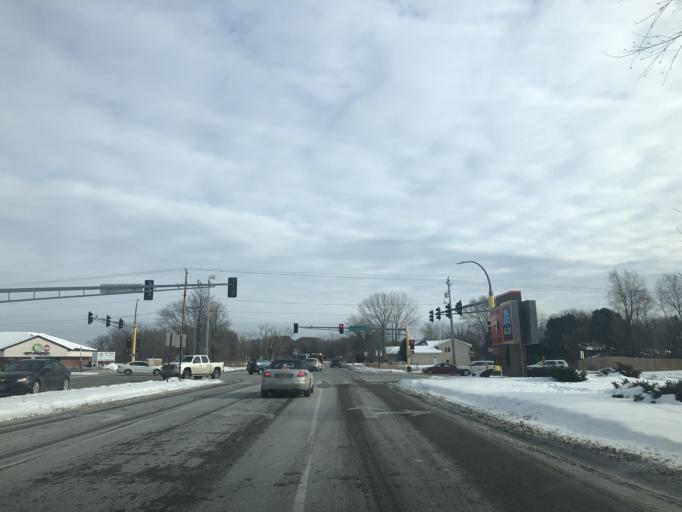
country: US
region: Minnesota
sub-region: Anoka County
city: Lexington
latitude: 45.1566
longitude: -93.1641
